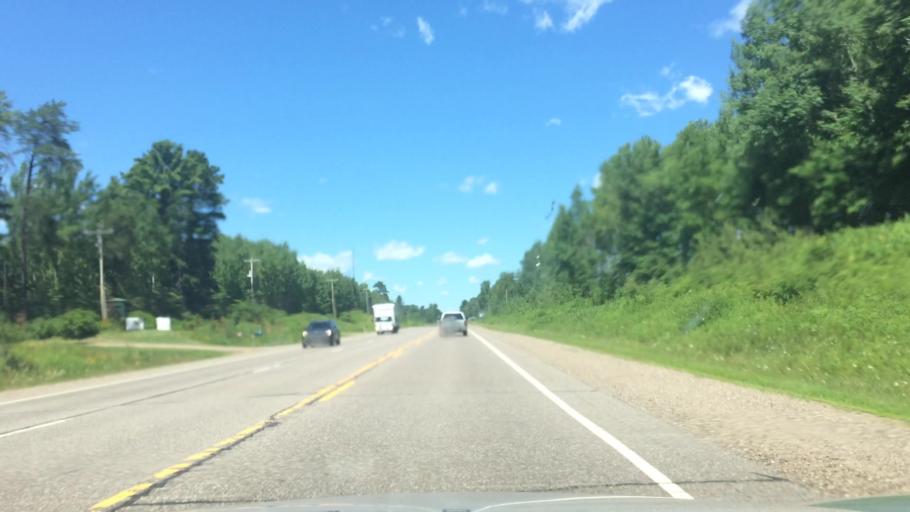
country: US
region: Wisconsin
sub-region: Lincoln County
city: Tomahawk
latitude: 45.6761
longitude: -89.7141
